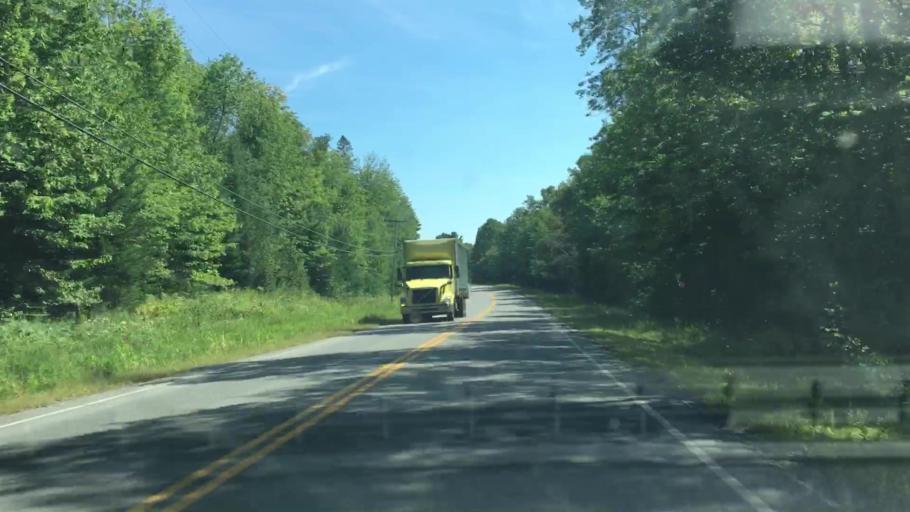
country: US
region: Maine
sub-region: Piscataquis County
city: Milo
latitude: 45.1964
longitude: -68.9034
